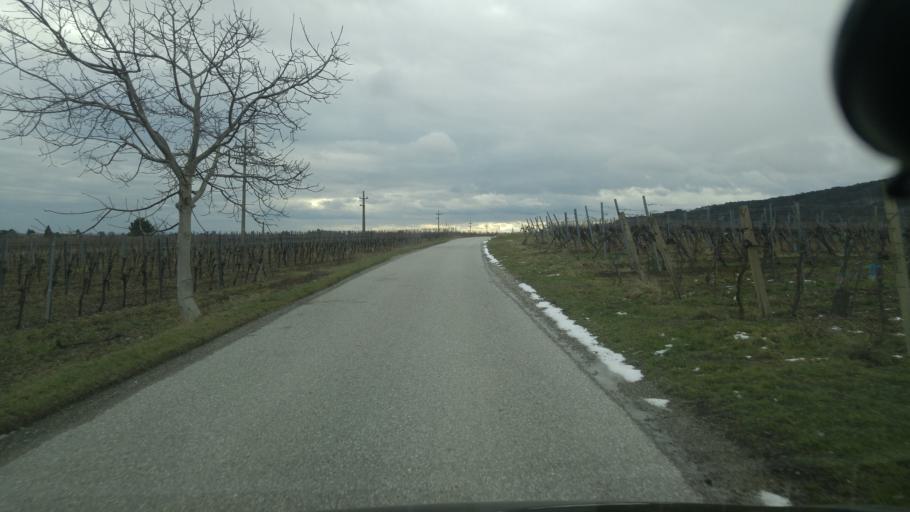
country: AT
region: Lower Austria
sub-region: Politischer Bezirk Baden
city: Bad Voslau
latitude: 47.9824
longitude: 16.2084
